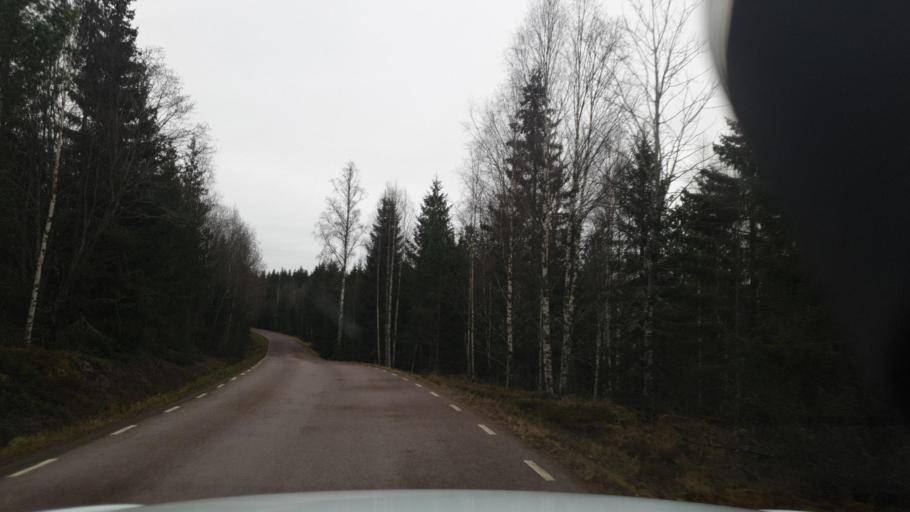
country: SE
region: Vaermland
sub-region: Karlstads Kommun
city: Valberg
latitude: 59.4567
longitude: 13.0838
